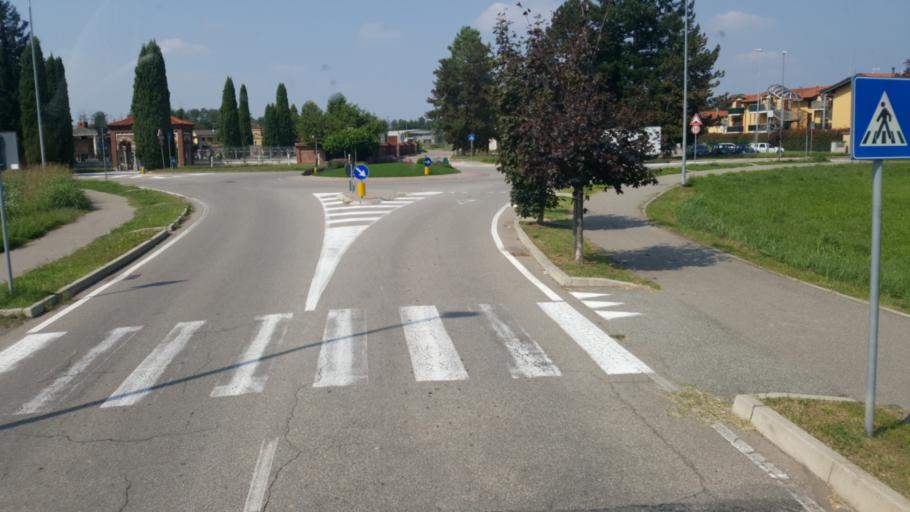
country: IT
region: Lombardy
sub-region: Provincia di Como
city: Carbonate
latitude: 45.6794
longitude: 8.9356
